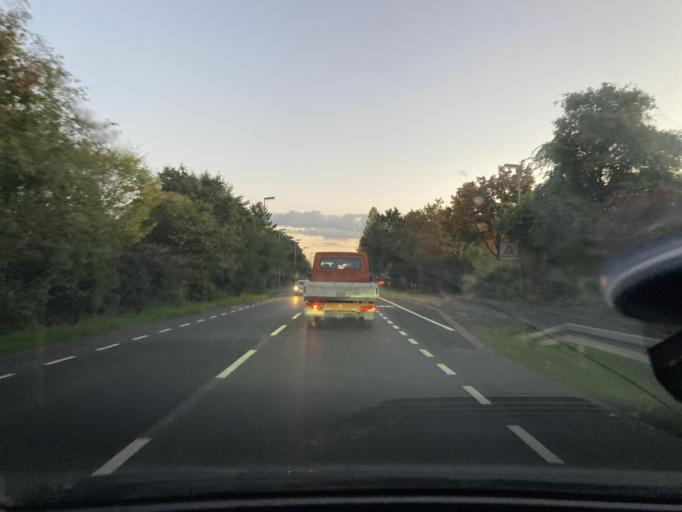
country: DE
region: Hesse
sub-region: Regierungsbezirk Darmstadt
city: Dietzenbach
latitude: 50.0259
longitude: 8.7848
